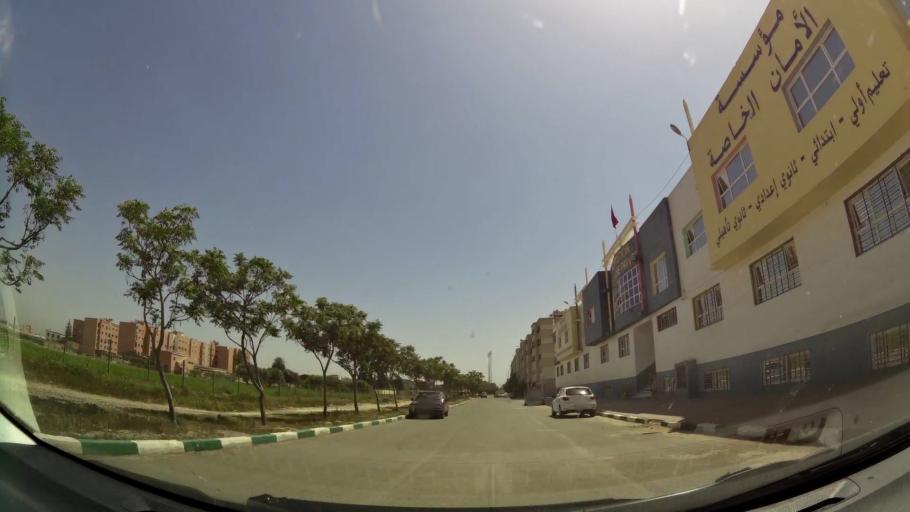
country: MA
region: Souss-Massa-Draa
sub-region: Inezgane-Ait Mellou
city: Inezgane
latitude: 30.3441
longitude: -9.5141
